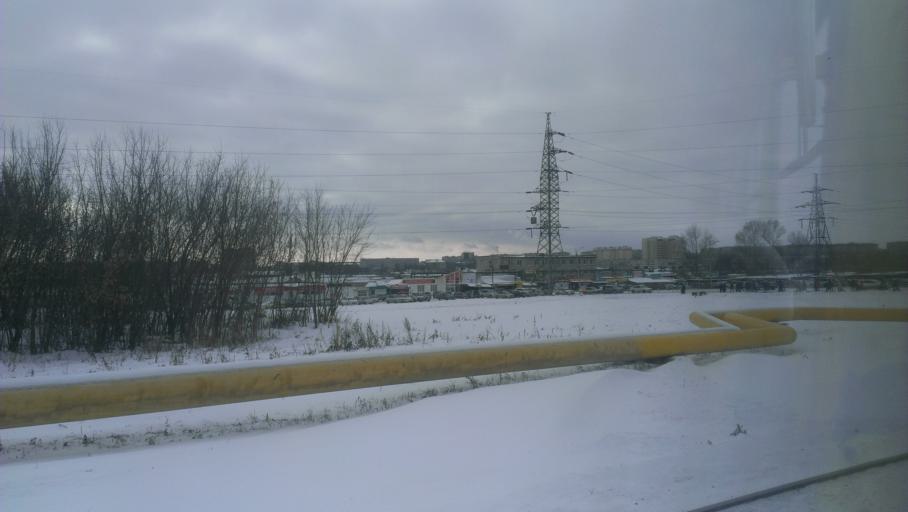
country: RU
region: Altai Krai
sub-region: Gorod Barnaulskiy
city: Barnaul
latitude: 53.3872
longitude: 83.6930
